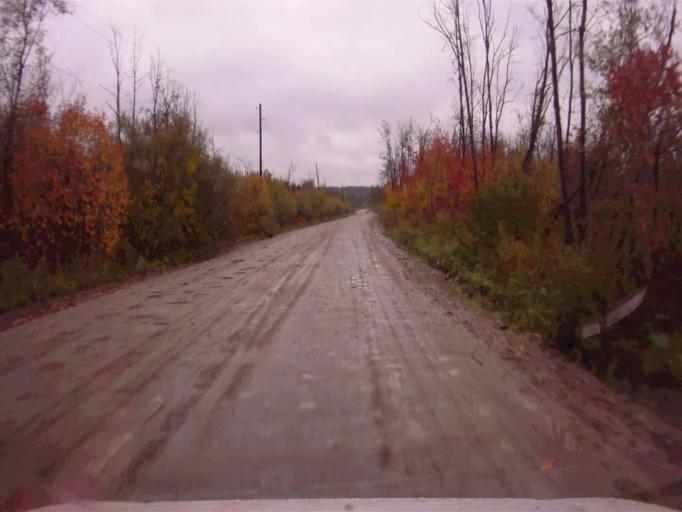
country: RU
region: Chelyabinsk
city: Kyshtym
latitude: 55.7342
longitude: 60.5166
